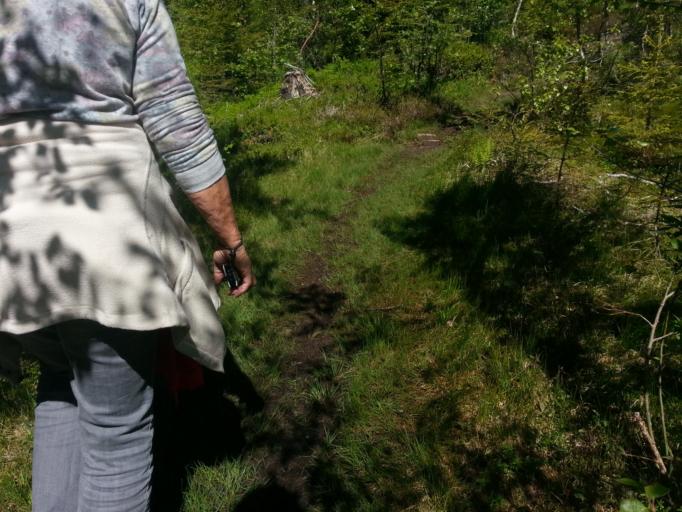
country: NO
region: Sor-Trondelag
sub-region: Trondheim
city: Trondheim
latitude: 63.4032
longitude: 10.2834
